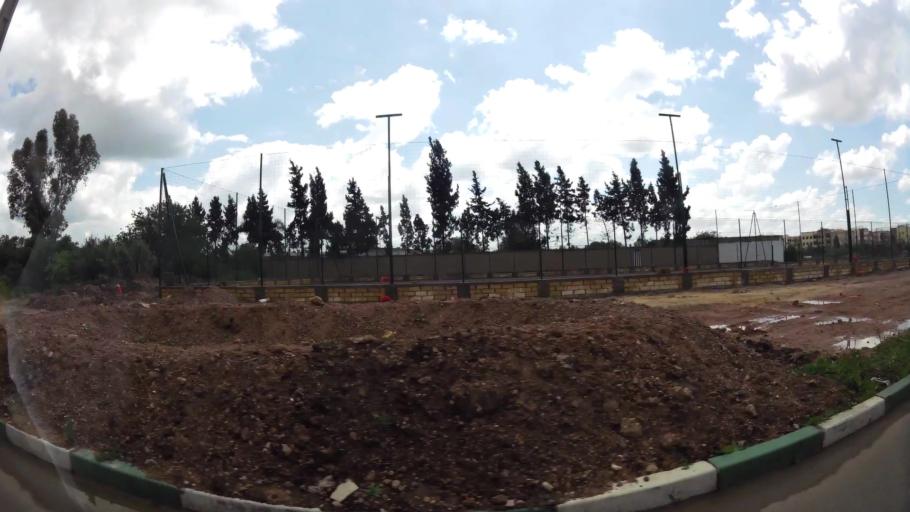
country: MA
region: Grand Casablanca
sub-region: Mediouna
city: Mediouna
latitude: 33.3879
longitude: -7.5406
